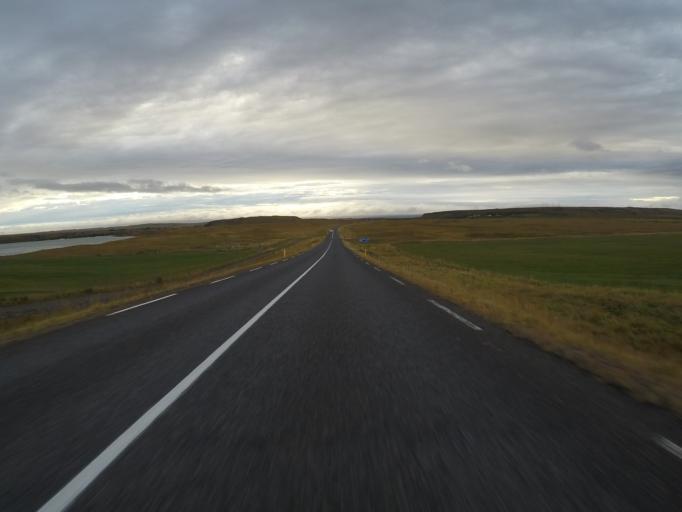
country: IS
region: South
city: Vestmannaeyjar
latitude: 64.0463
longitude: -20.1582
